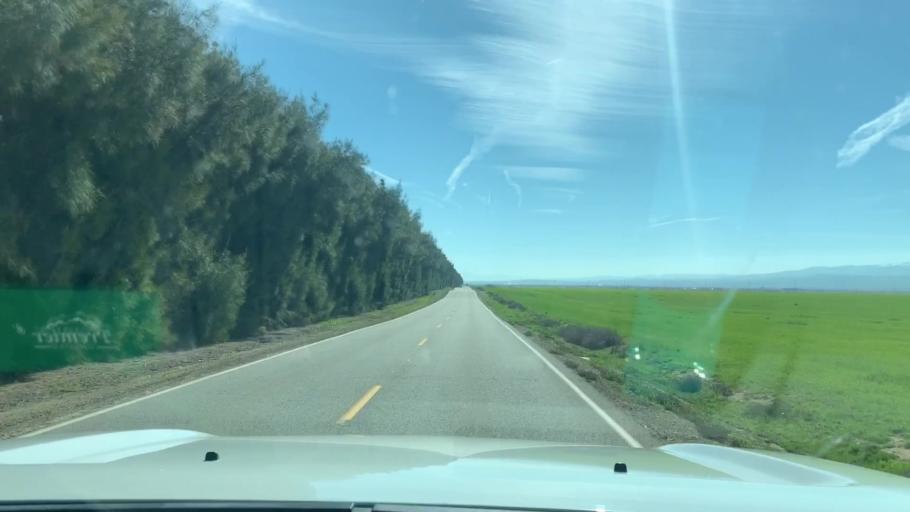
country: US
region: California
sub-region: Kern County
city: Lost Hills
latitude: 35.5132
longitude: -119.7495
